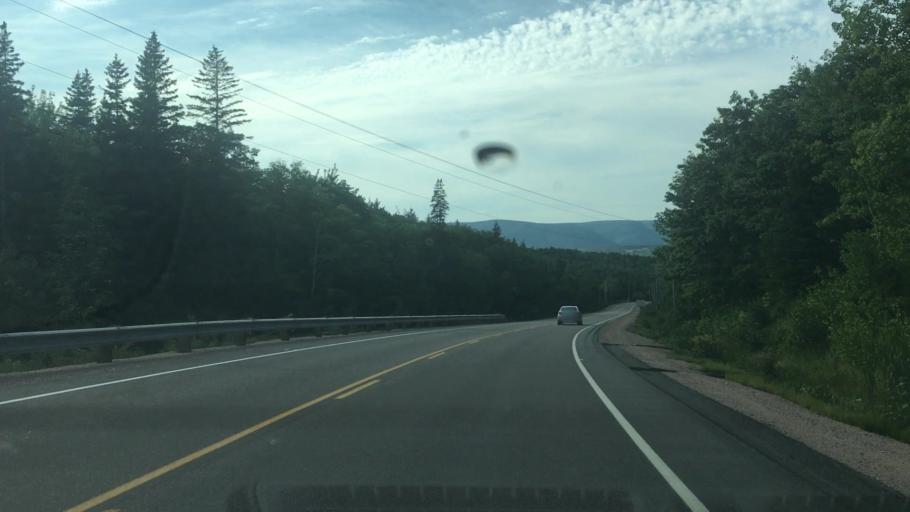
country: CA
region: Nova Scotia
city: Sydney Mines
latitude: 46.8557
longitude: -60.4574
